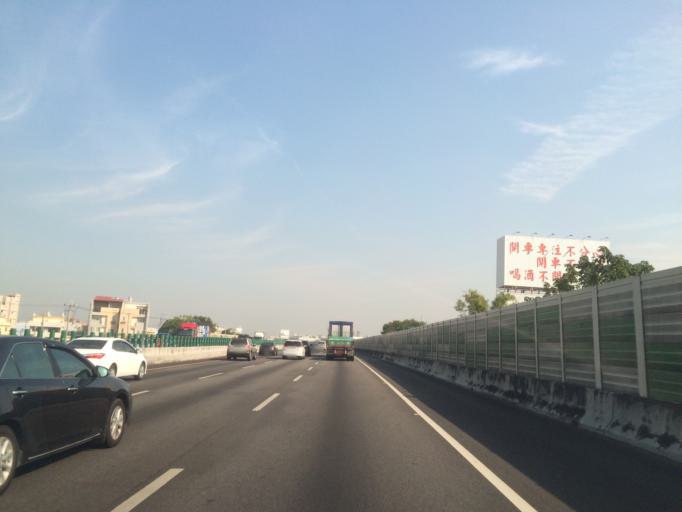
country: TW
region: Taiwan
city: Fengyuan
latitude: 24.2199
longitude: 120.6797
